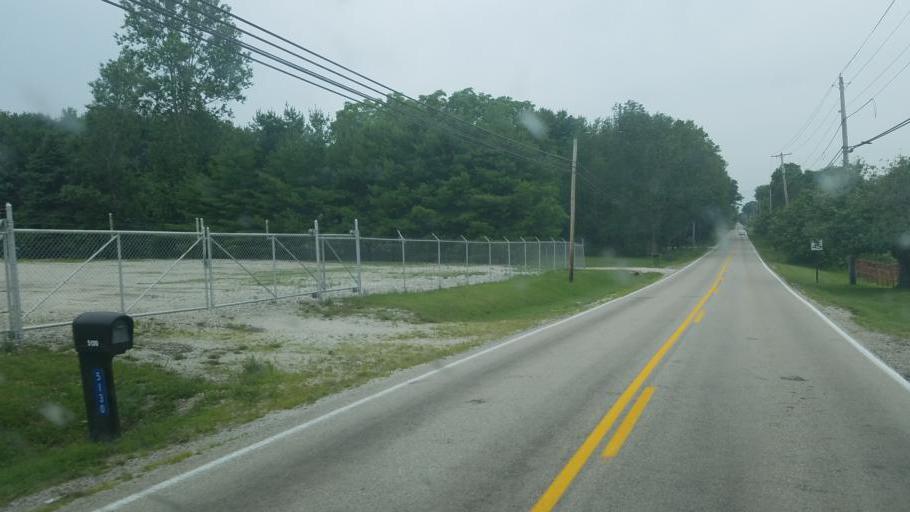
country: US
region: Ohio
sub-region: Portage County
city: Ravenna
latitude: 41.0985
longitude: -81.2074
